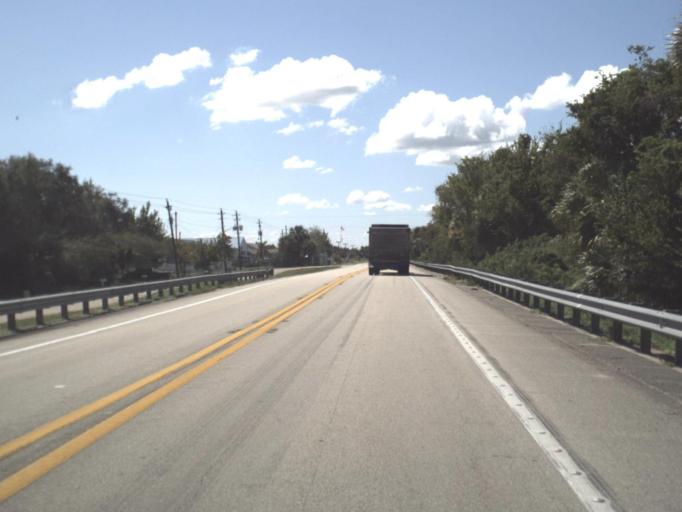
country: US
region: Florida
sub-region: Glades County
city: Buckhead Ridge
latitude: 27.1377
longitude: -80.8902
